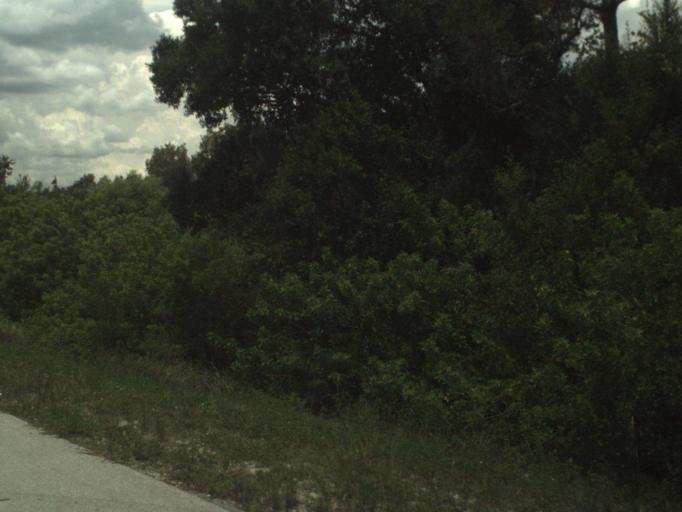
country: US
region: Florida
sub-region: Saint Lucie County
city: Lakewood Park
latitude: 27.5486
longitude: -80.3700
